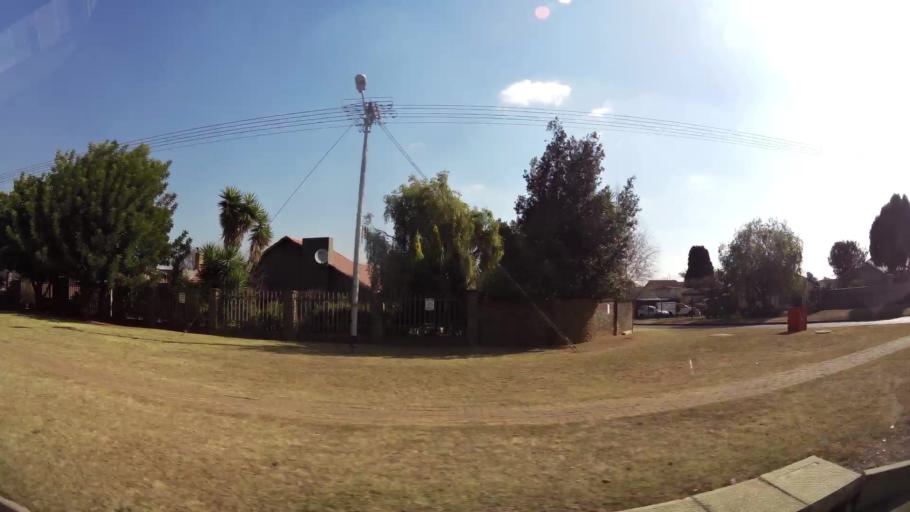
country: ZA
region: Gauteng
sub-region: West Rand District Municipality
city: Randfontein
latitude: -26.1565
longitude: 27.6918
